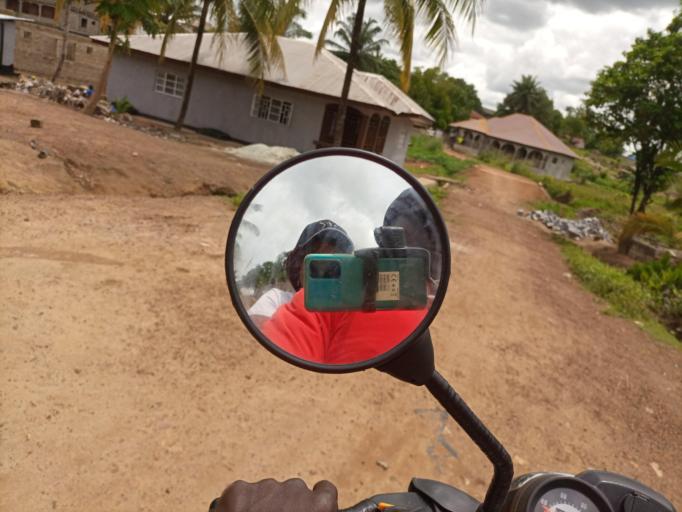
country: SL
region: Southern Province
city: Bo
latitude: 7.9700
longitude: -11.7181
